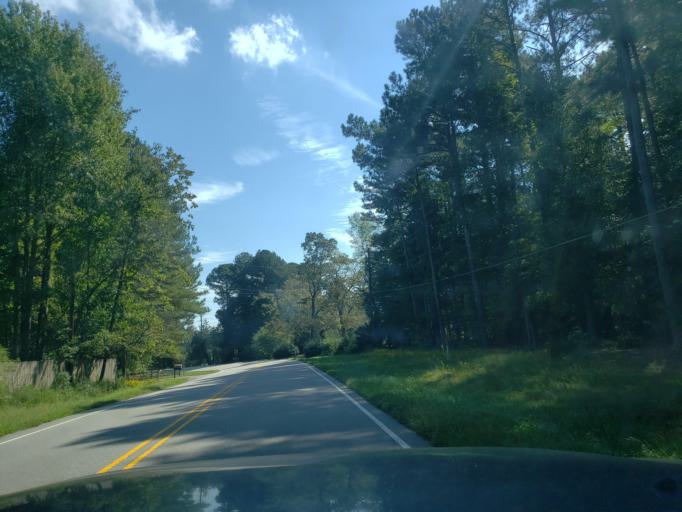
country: US
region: North Carolina
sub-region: Wake County
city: West Raleigh
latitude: 35.9328
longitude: -78.7071
